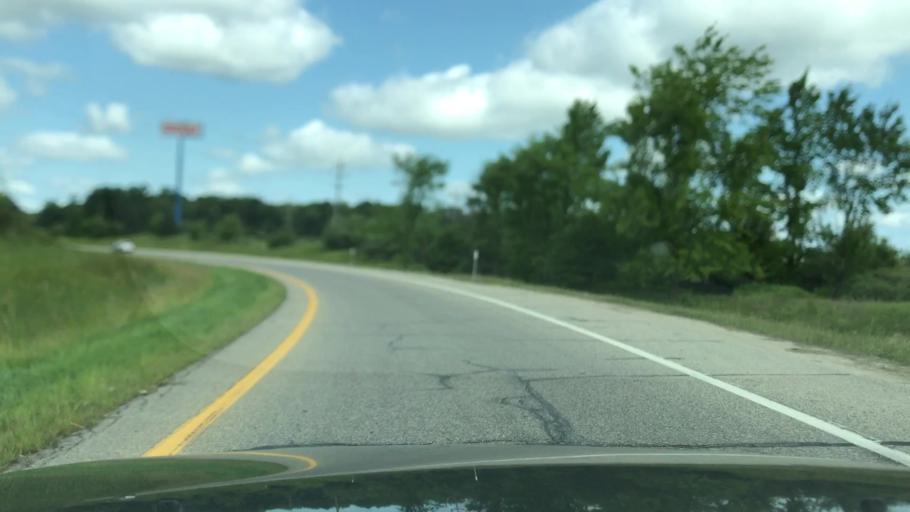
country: US
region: Michigan
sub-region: Mecosta County
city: Big Rapids
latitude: 43.6882
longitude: -85.5183
